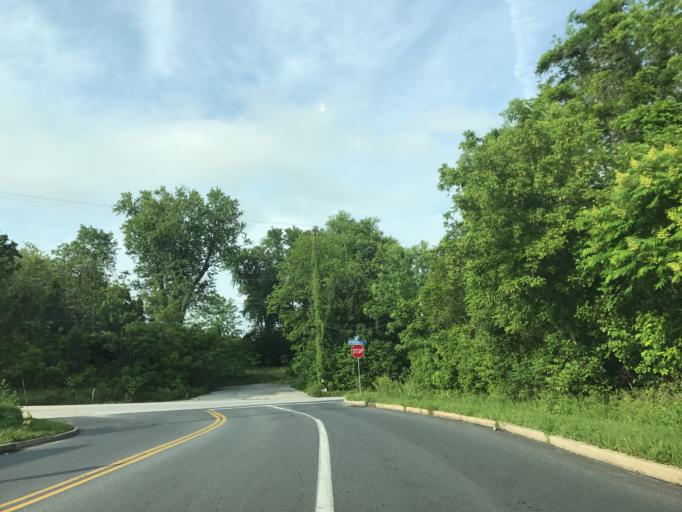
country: US
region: Pennsylvania
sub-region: York County
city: Spry
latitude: 39.9365
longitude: -76.6812
